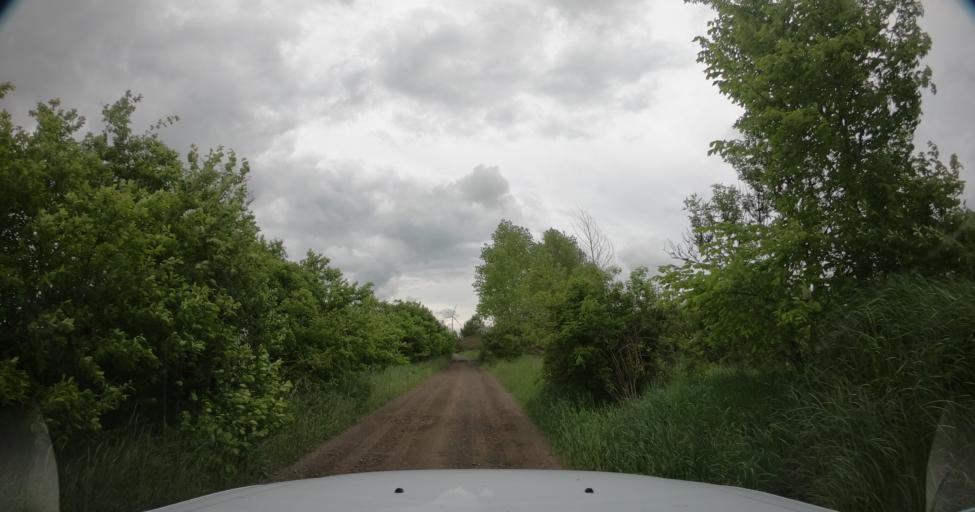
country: PL
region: West Pomeranian Voivodeship
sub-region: Powiat pyrzycki
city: Kozielice
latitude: 53.1055
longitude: 14.8117
